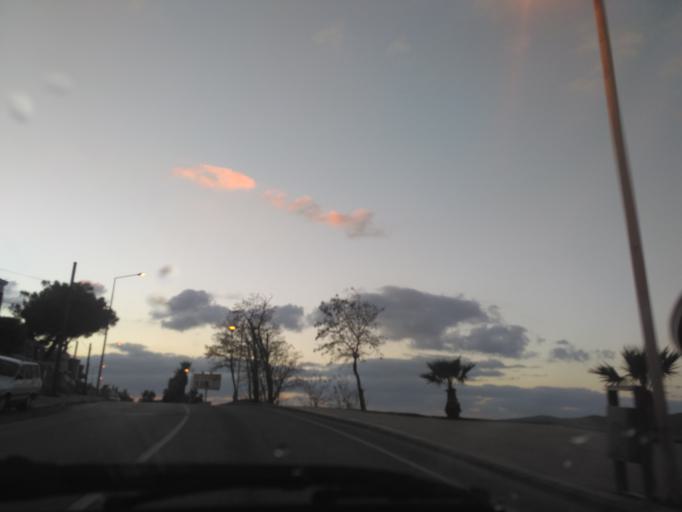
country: TR
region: Balikesir
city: Ayvalik
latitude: 39.3120
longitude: 26.6827
